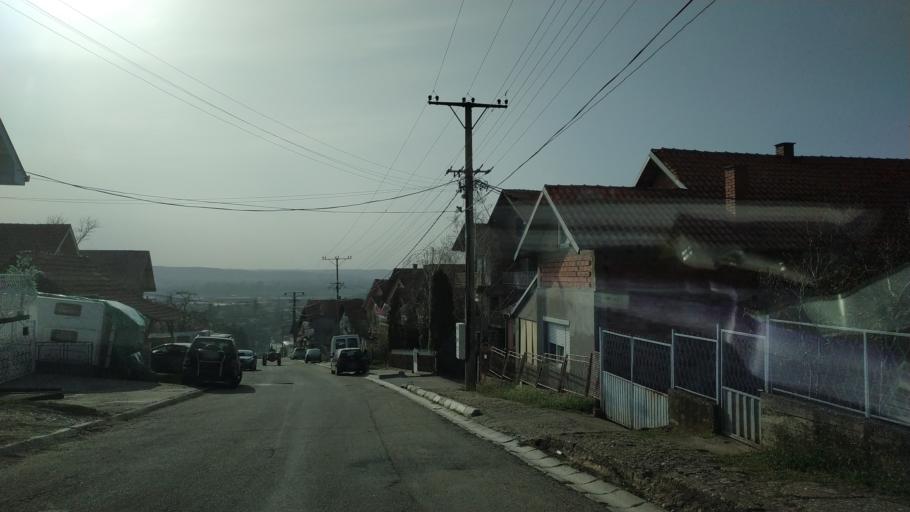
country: RS
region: Central Serbia
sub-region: Nisavski Okrug
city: Aleksinac
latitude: 43.5363
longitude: 21.7157
